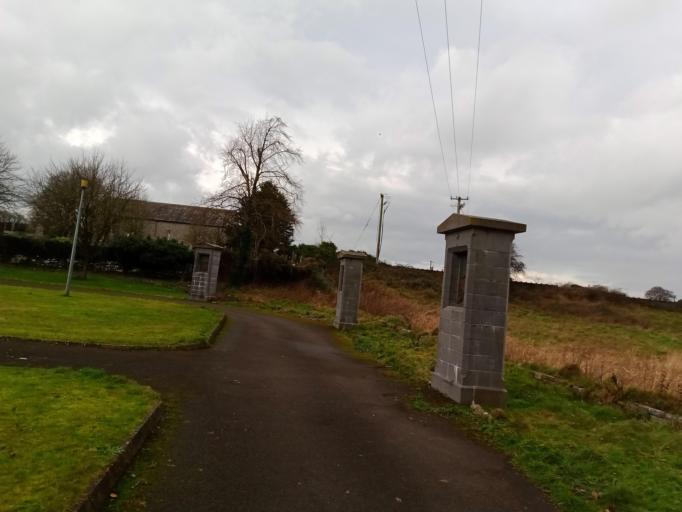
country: IE
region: Munster
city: Thurles
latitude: 52.6401
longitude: -7.8671
